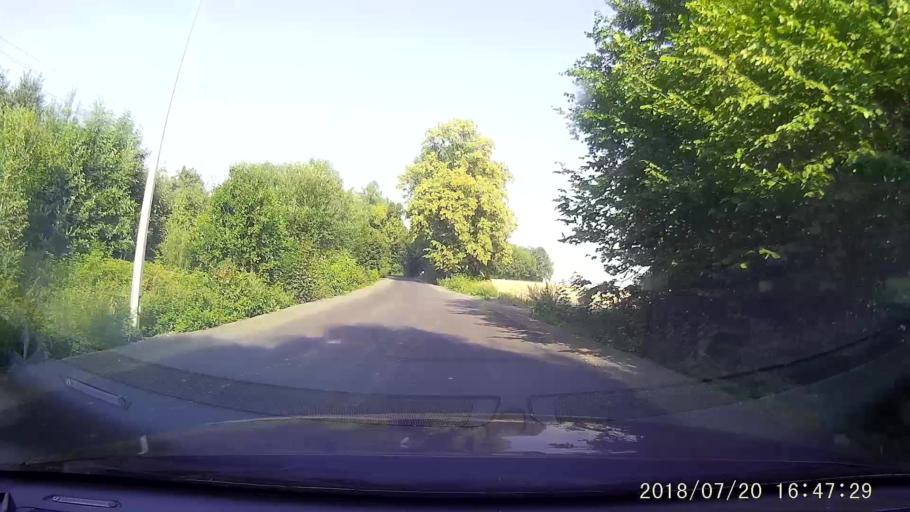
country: PL
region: Lower Silesian Voivodeship
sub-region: Powiat lubanski
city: Siekierczyn
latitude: 51.0596
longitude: 15.1787
